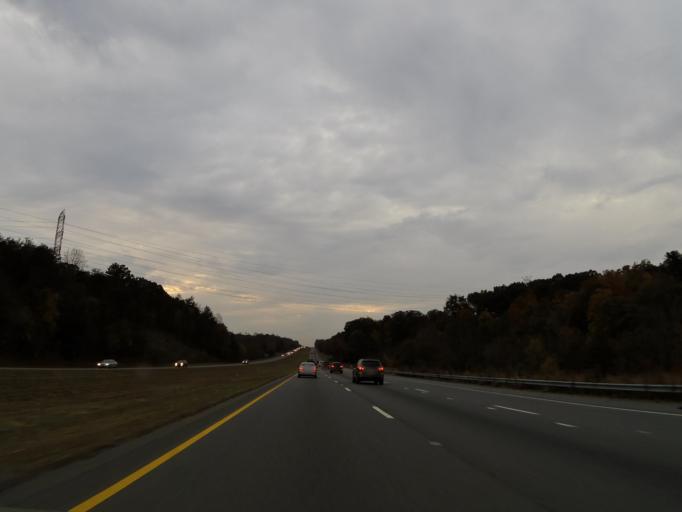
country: US
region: North Carolina
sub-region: Burke County
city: Hildebran
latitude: 35.7061
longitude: -81.3989
